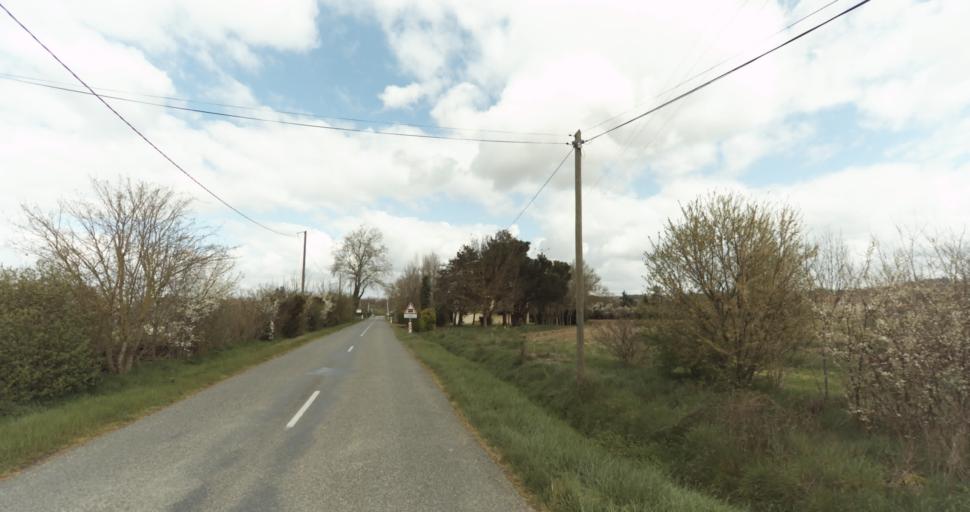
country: FR
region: Midi-Pyrenees
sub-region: Departement de la Haute-Garonne
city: Auterive
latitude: 43.3348
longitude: 1.4792
